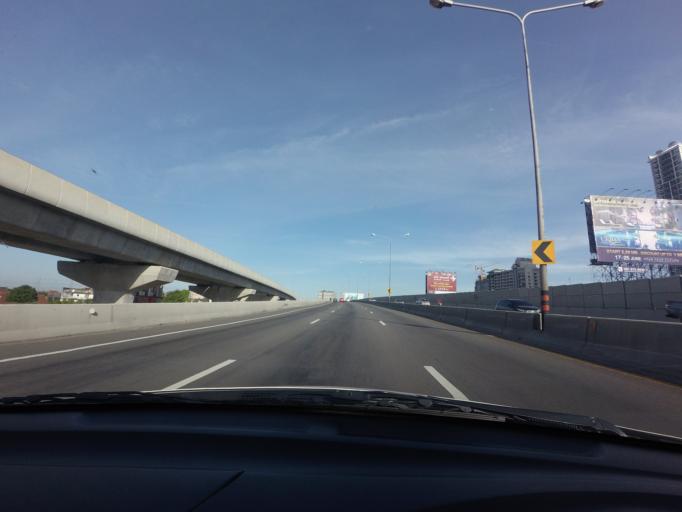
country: TH
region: Nonthaburi
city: Mueang Nonthaburi
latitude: 13.8707
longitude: 100.4836
